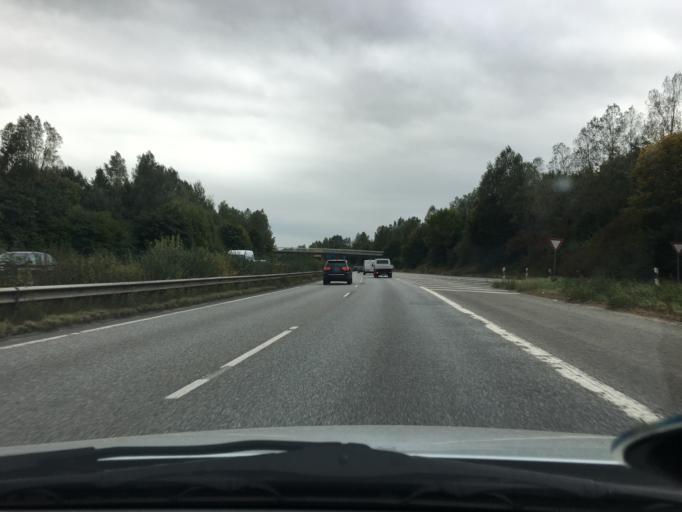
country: DE
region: Schleswig-Holstein
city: Kronshagen
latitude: 54.3276
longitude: 10.0986
